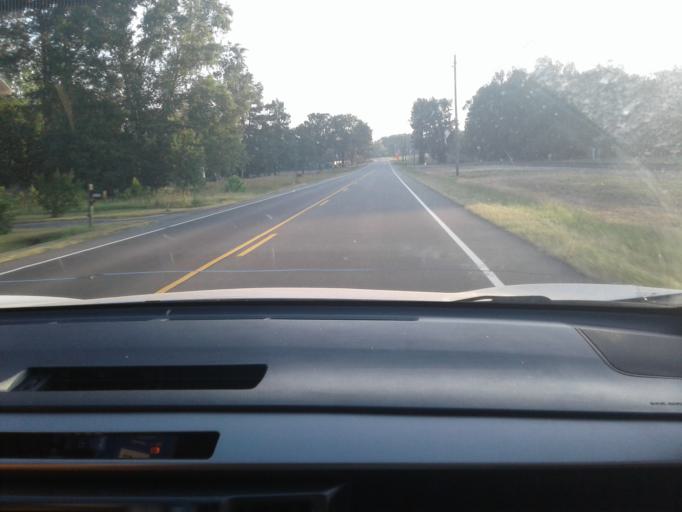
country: US
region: North Carolina
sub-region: Harnett County
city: Angier
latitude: 35.4855
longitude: -78.8179
